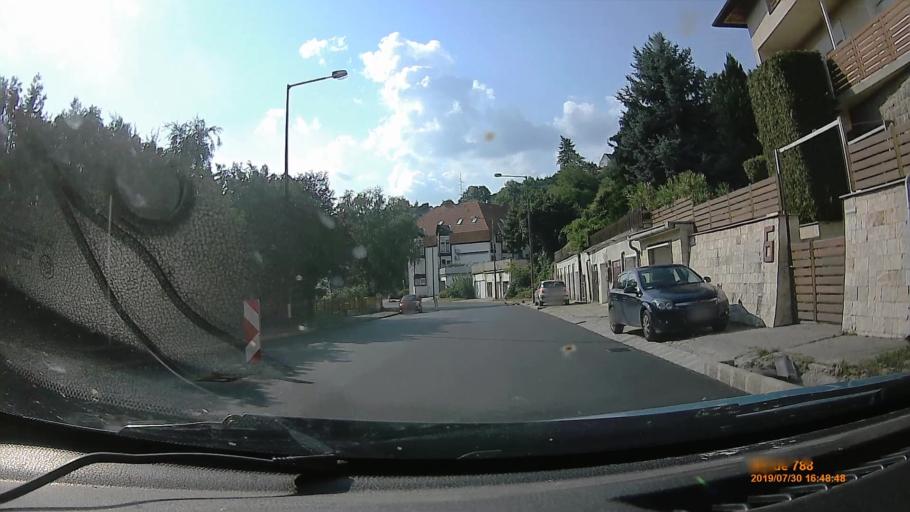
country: HU
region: Baranya
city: Pecs
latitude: 46.0833
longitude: 18.2160
